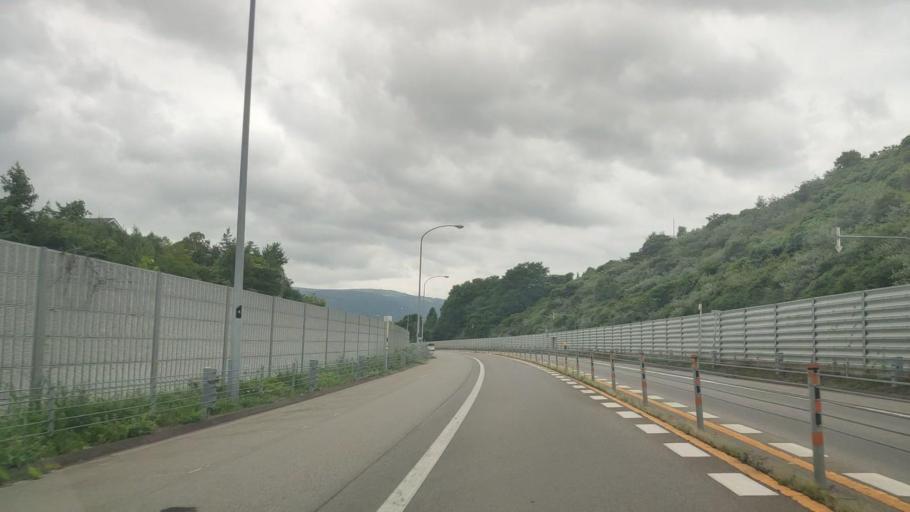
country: JP
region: Hokkaido
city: Nanae
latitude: 41.9145
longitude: 140.6897
